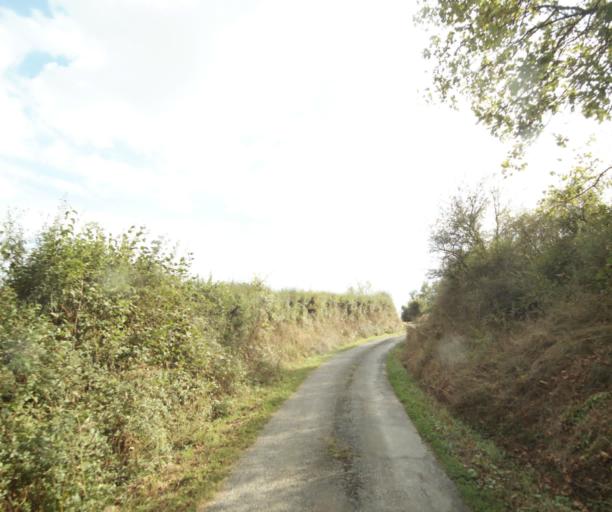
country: FR
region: Bourgogne
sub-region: Departement de Saone-et-Loire
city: Palinges
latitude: 46.5120
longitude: 4.2441
